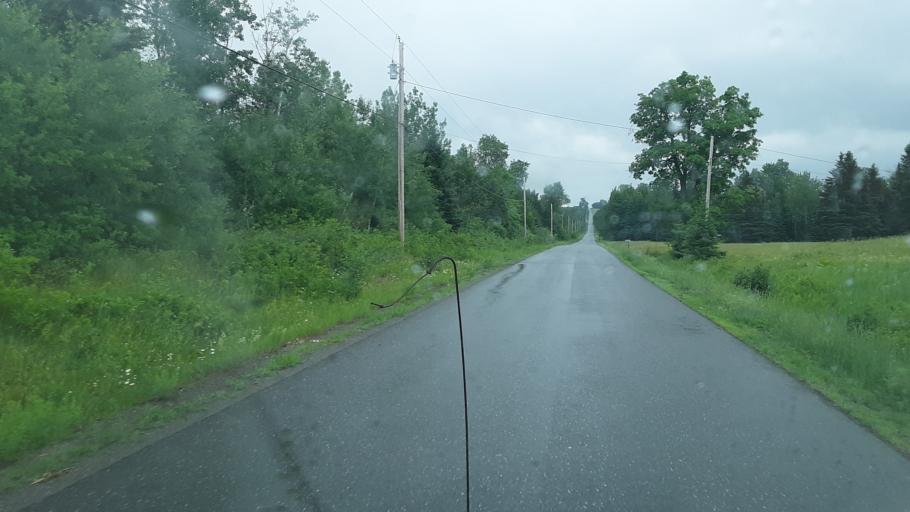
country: US
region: Maine
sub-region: Aroostook County
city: Presque Isle
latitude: 46.6813
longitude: -68.2110
